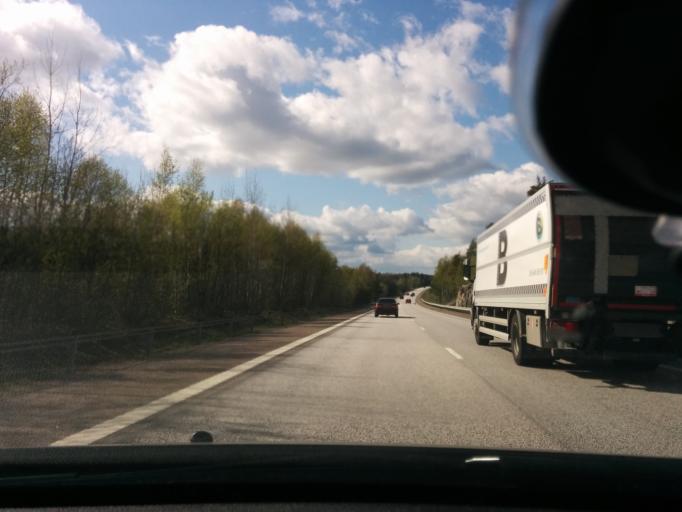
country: SE
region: Stockholm
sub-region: Upplands-Bro Kommun
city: Bro
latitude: 59.5124
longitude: 17.6851
